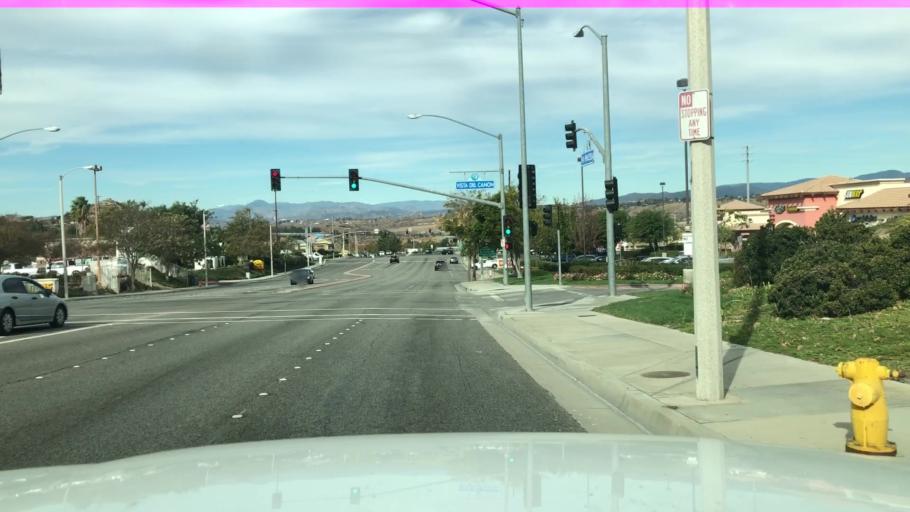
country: US
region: California
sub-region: Los Angeles County
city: Santa Clarita
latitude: 34.4043
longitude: -118.4630
